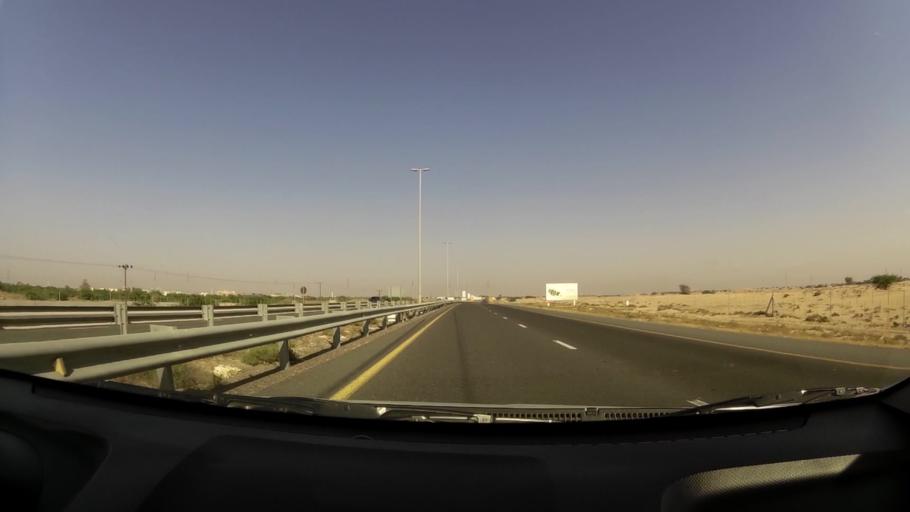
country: AE
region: Umm al Qaywayn
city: Umm al Qaywayn
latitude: 25.4763
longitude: 55.5712
